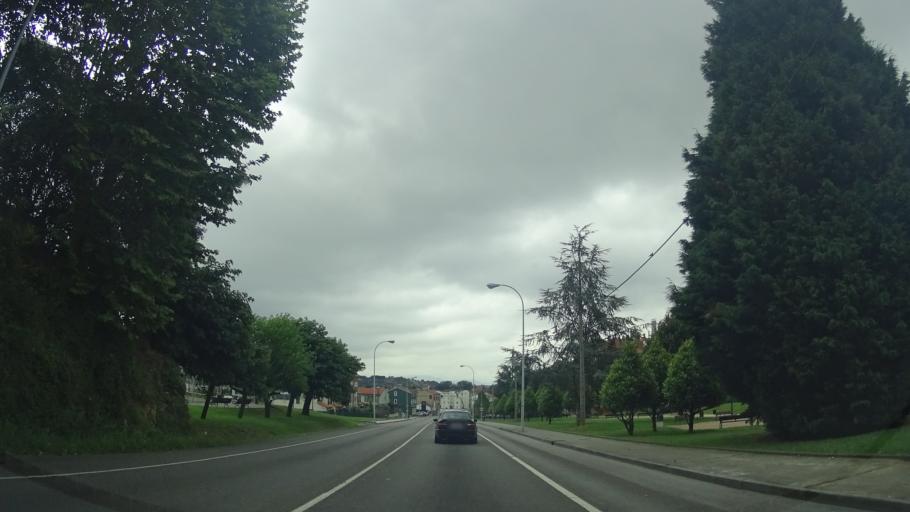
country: ES
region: Asturias
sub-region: Province of Asturias
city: Lugones
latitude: 43.3782
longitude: -5.7975
